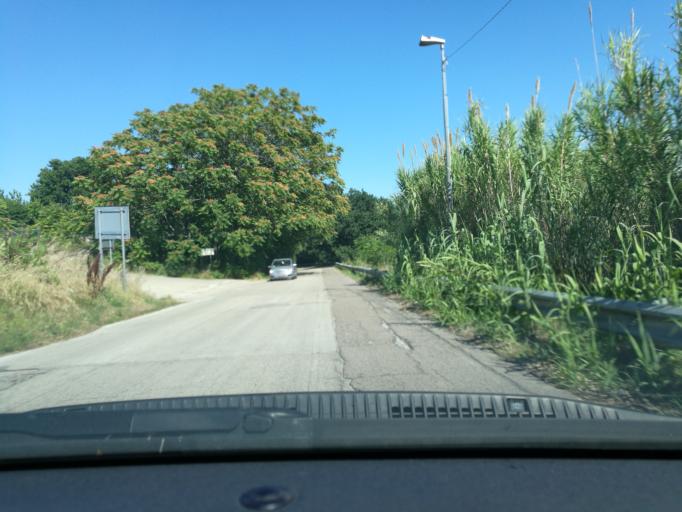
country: IT
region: Abruzzo
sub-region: Provincia di Chieti
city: Vasto
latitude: 42.1664
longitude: 14.6950
